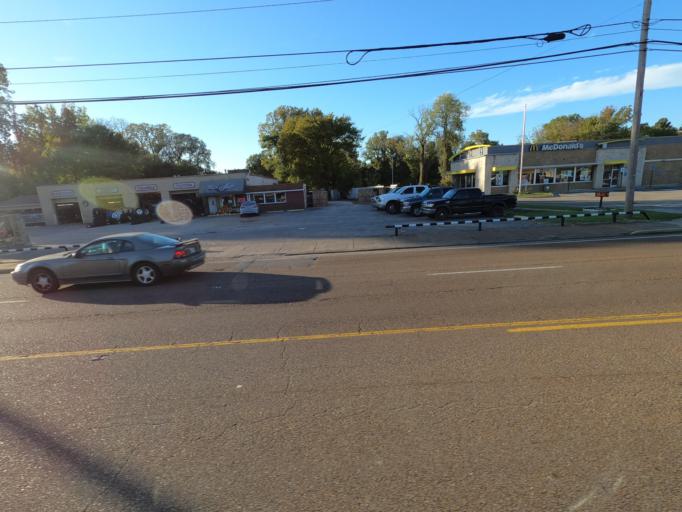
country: US
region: Tennessee
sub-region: Shelby County
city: Millington
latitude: 35.3400
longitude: -89.9115
